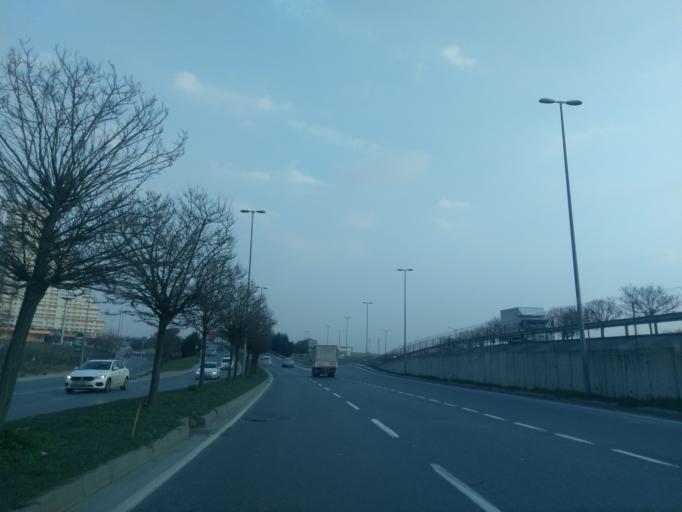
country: TR
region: Istanbul
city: Esenyurt
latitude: 41.0572
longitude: 28.7125
